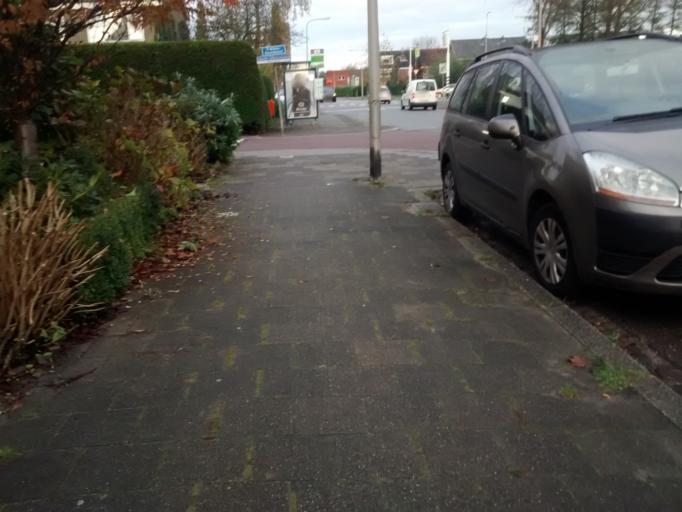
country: NL
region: South Holland
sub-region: Gemeente Gouda
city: Bloemendaal
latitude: 52.0234
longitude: 4.6977
